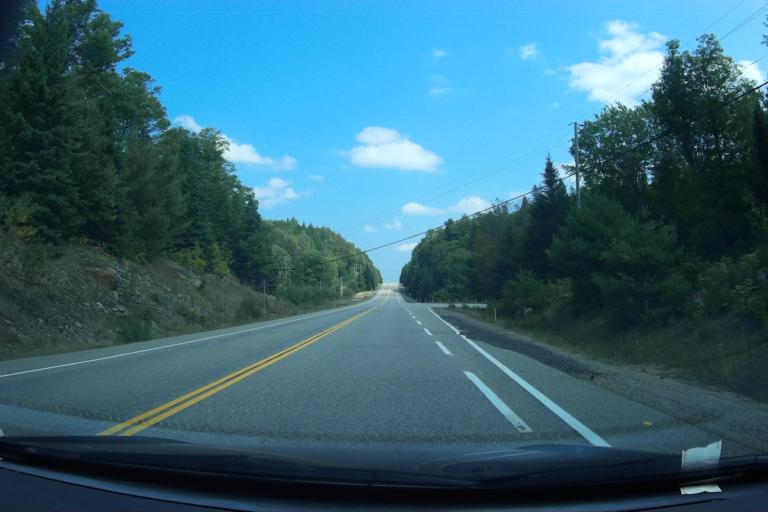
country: CA
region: Ontario
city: Huntsville
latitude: 45.5642
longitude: -78.5443
